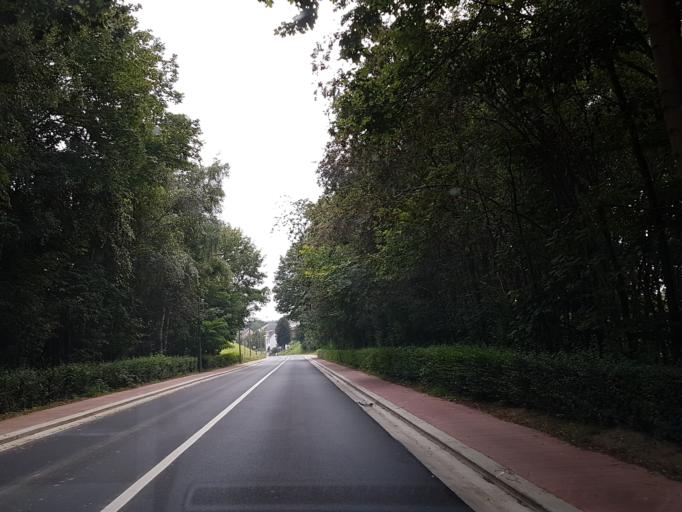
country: BE
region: Flanders
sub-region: Provincie Vlaams-Brabant
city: Kortenberg
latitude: 50.8687
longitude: 4.5196
